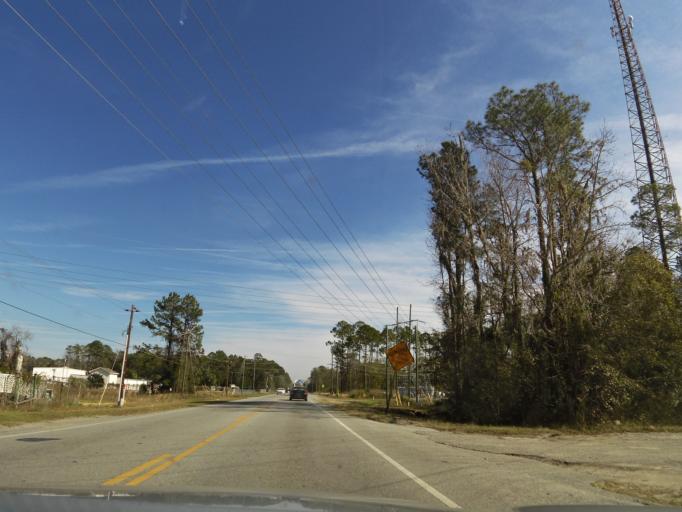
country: US
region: Georgia
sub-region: Glynn County
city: Dock Junction
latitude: 31.2724
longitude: -81.5547
